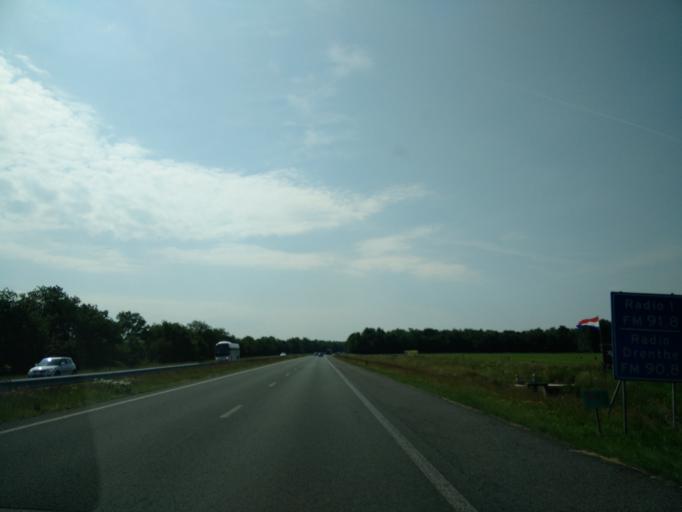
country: NL
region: Drenthe
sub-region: Gemeente Tynaarlo
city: Tynaarlo
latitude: 53.1081
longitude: 6.6119
